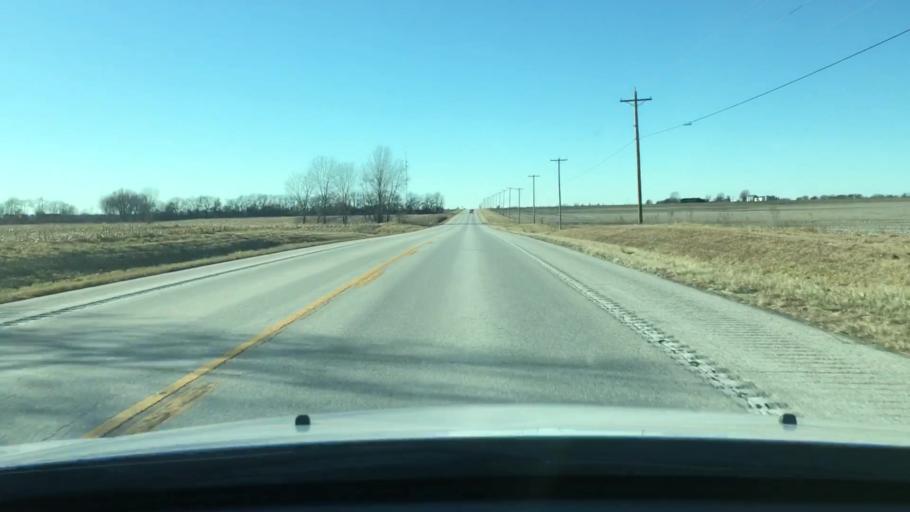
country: US
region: Missouri
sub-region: Pike County
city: Bowling Green
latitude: 39.3445
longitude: -91.2842
